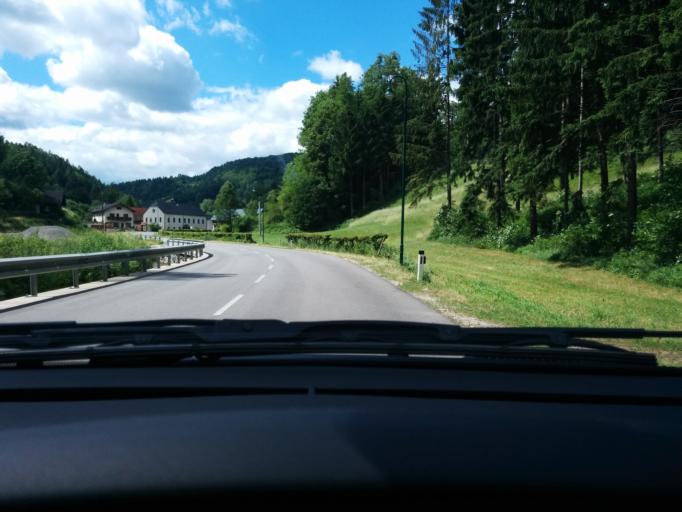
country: AT
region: Lower Austria
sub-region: Politischer Bezirk Wiener Neustadt
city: Miesenbach
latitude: 47.8504
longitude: 15.9874
